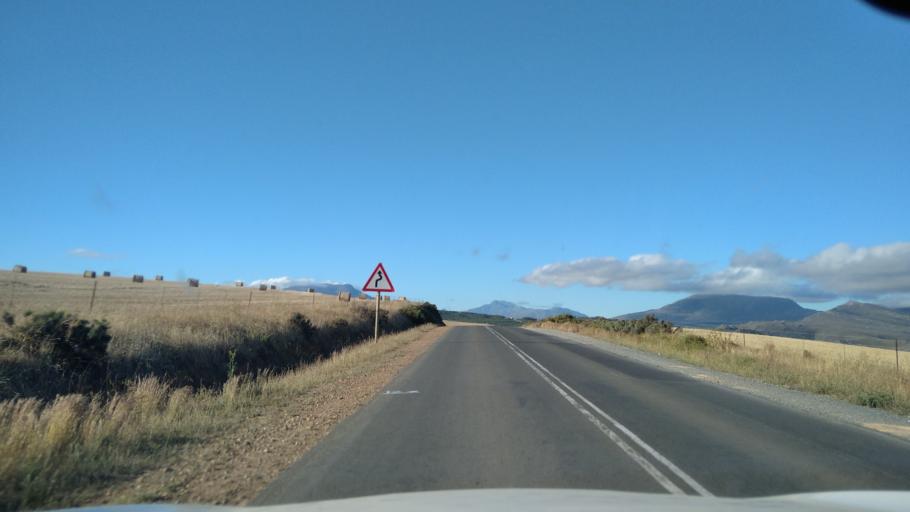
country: ZA
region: Western Cape
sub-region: Overberg District Municipality
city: Caledon
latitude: -34.1313
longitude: 19.2957
